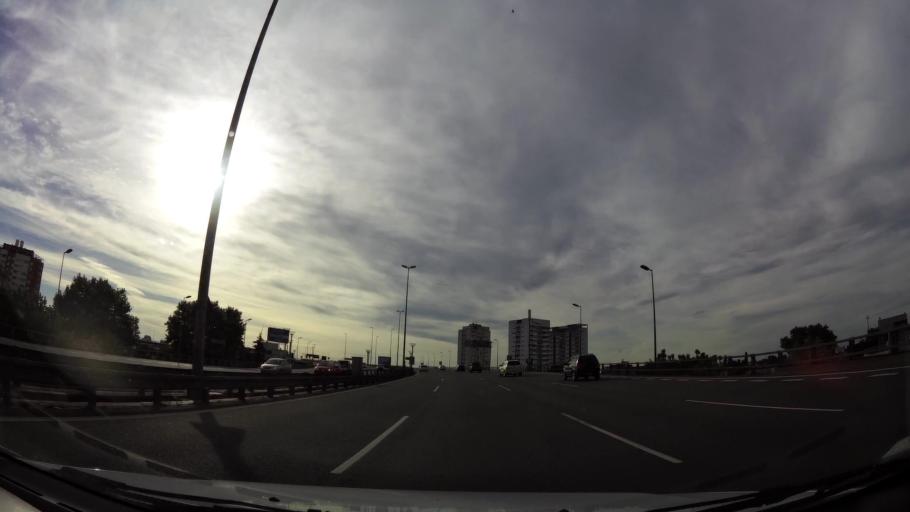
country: AR
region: Buenos Aires
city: Caseros
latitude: -34.6353
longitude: -58.5264
